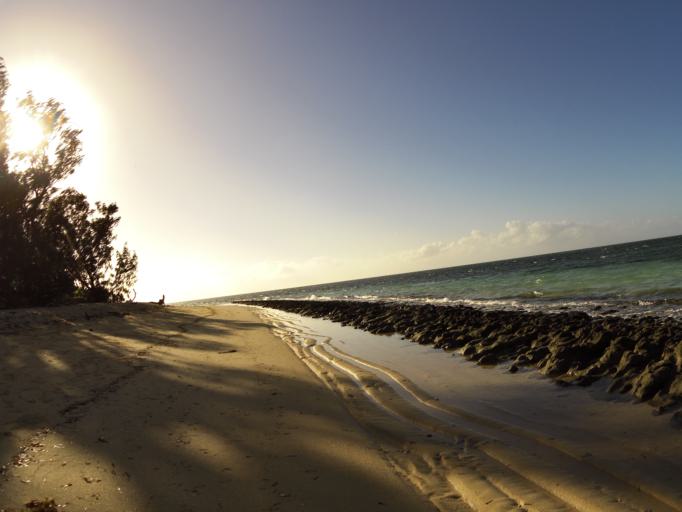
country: AU
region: Queensland
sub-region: Cairns
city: Yorkeys Knob
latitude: -16.7606
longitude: 145.9761
